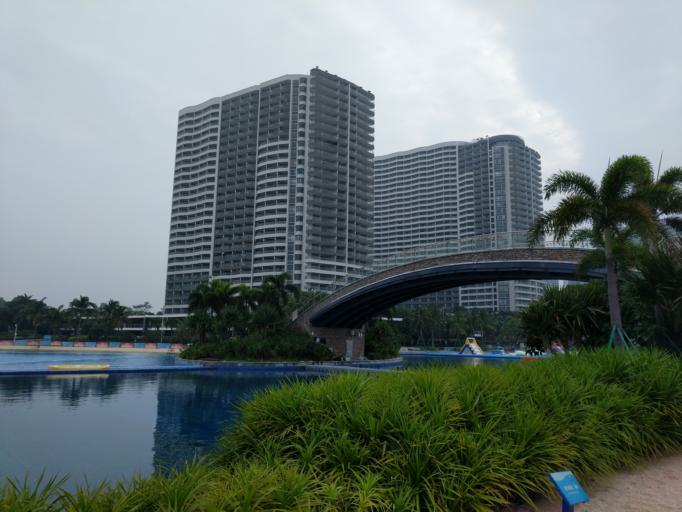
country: CN
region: Guangdong
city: Pinggang
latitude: 21.6138
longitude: 111.9379
